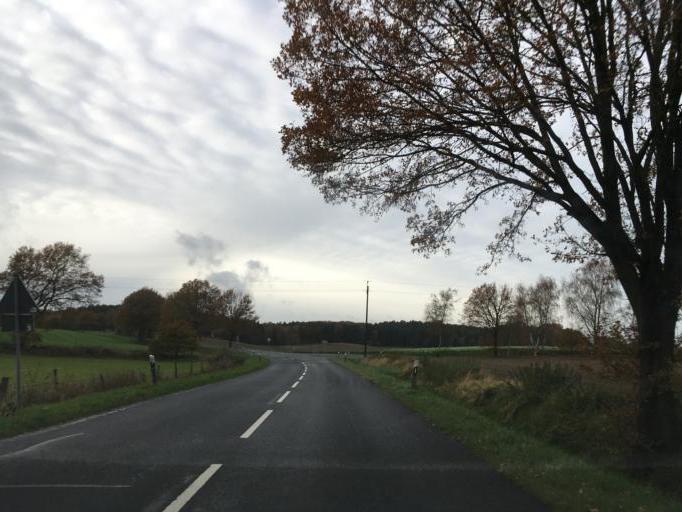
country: DE
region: Lower Saxony
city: Eyendorf
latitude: 53.1757
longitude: 10.1785
